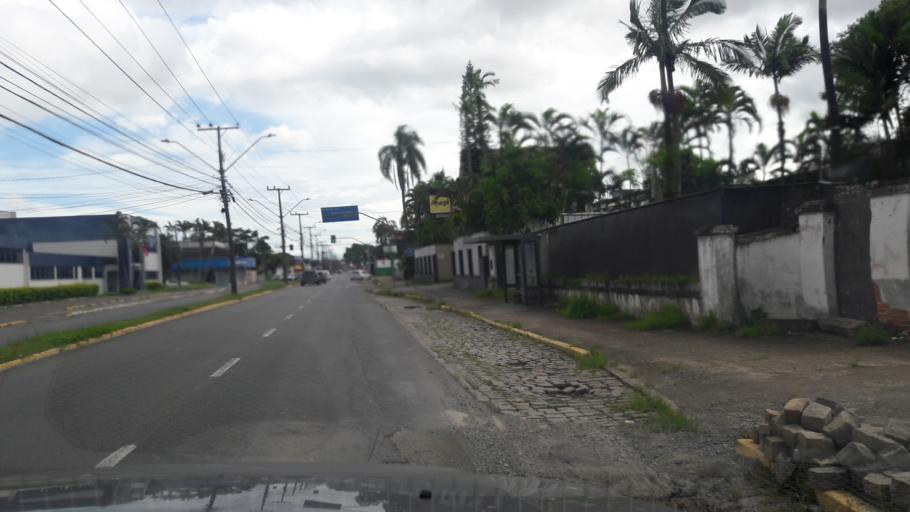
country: BR
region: Santa Catarina
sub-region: Joinville
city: Joinville
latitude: -26.3135
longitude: -48.8407
